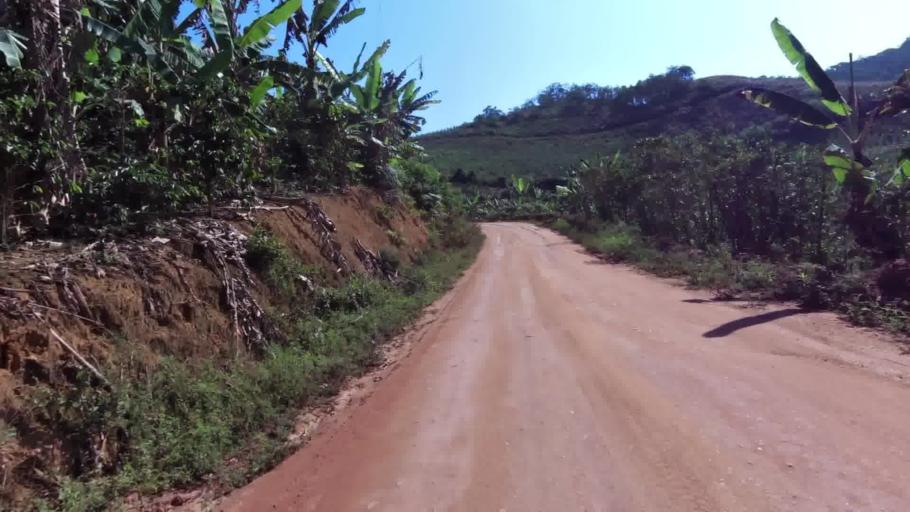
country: BR
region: Espirito Santo
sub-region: Alfredo Chaves
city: Alfredo Chaves
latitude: -20.5641
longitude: -40.7751
